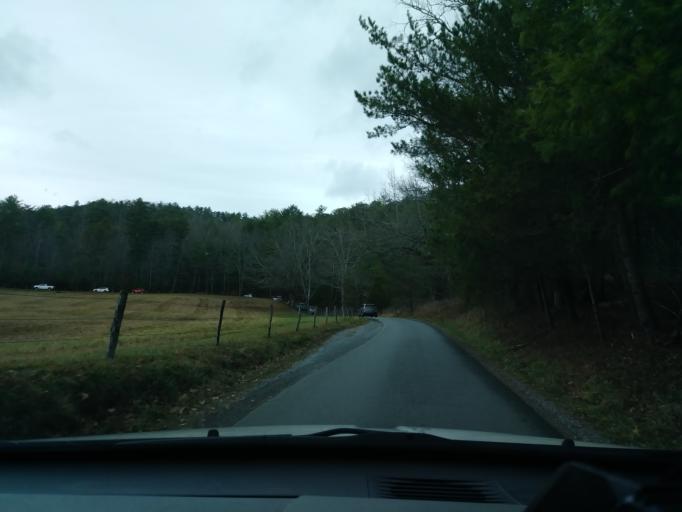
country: US
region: Tennessee
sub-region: Blount County
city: Wildwood
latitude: 35.6067
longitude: -83.8308
